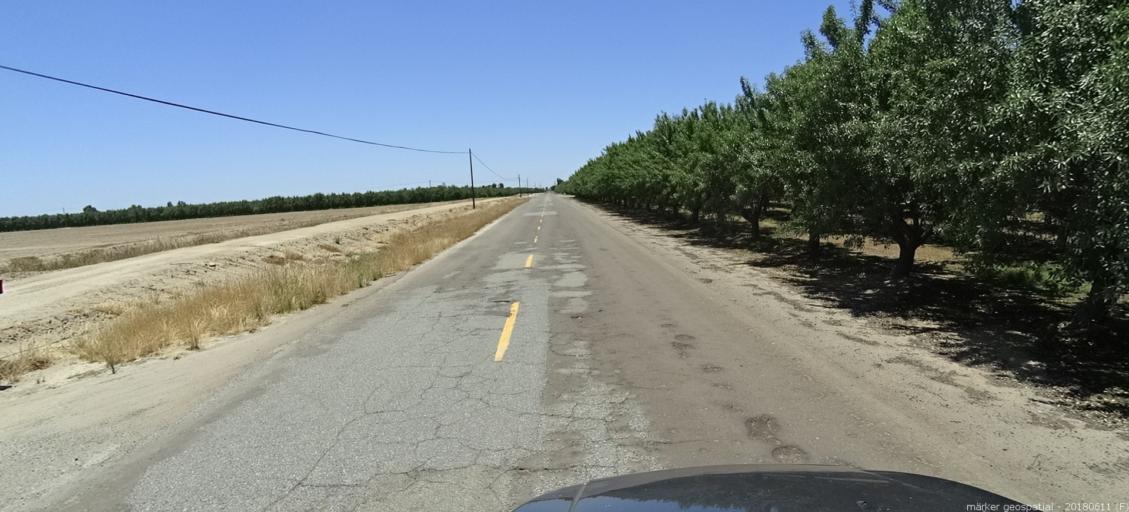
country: US
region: California
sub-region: Madera County
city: Fairmead
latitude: 37.0345
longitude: -120.1841
